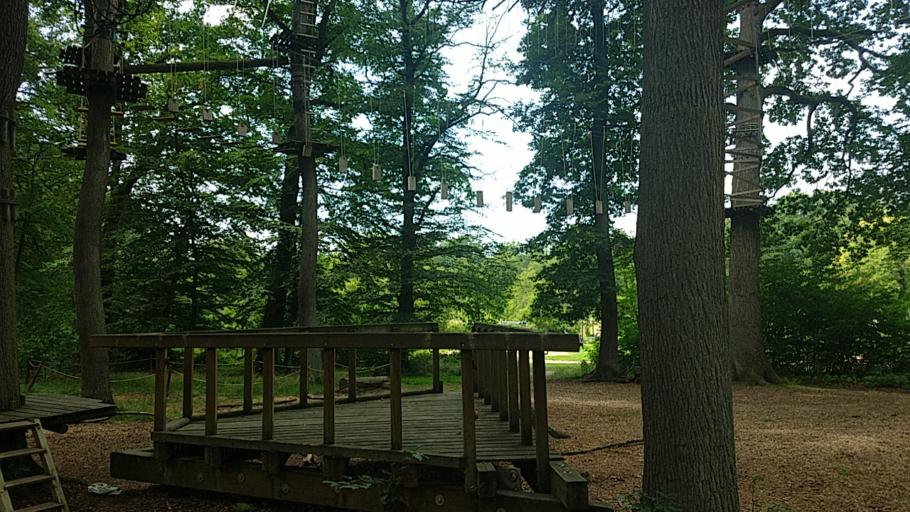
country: DE
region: Lower Saxony
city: Hameln
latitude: 52.0960
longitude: 9.3240
